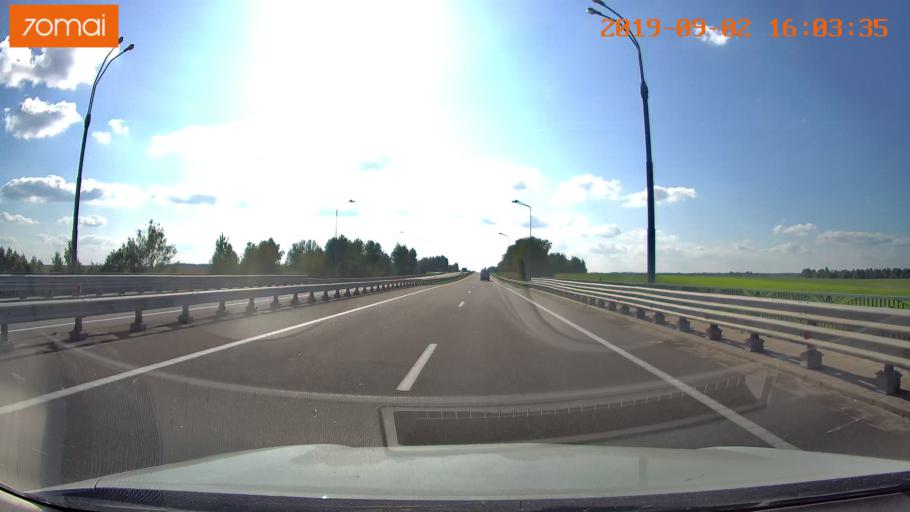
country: BY
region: Minsk
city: Byerazino
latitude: 53.8031
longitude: 28.8667
